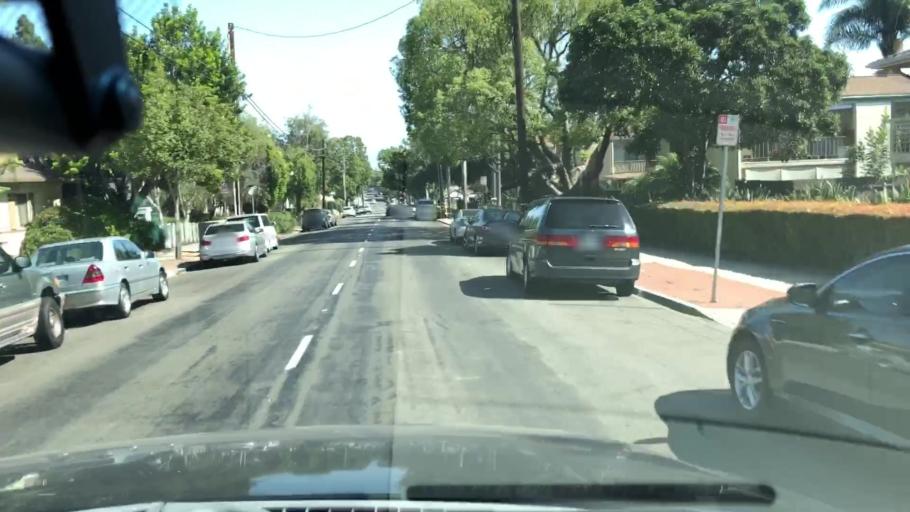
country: US
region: California
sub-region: Santa Barbara County
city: Mission Canyon
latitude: 34.4303
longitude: -119.7190
